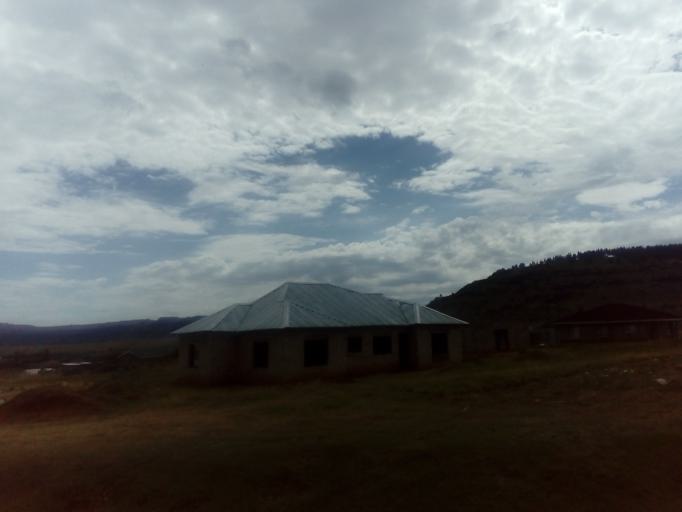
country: LS
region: Leribe
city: Maputsoe
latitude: -28.9500
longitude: 27.9598
